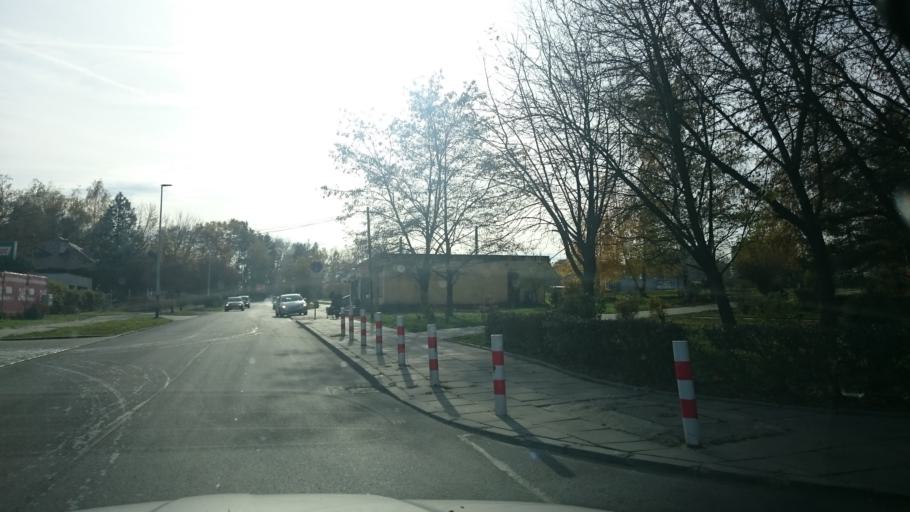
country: PL
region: Lesser Poland Voivodeship
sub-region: Powiat wielicki
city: Czarnochowice
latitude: 50.0164
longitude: 20.0246
